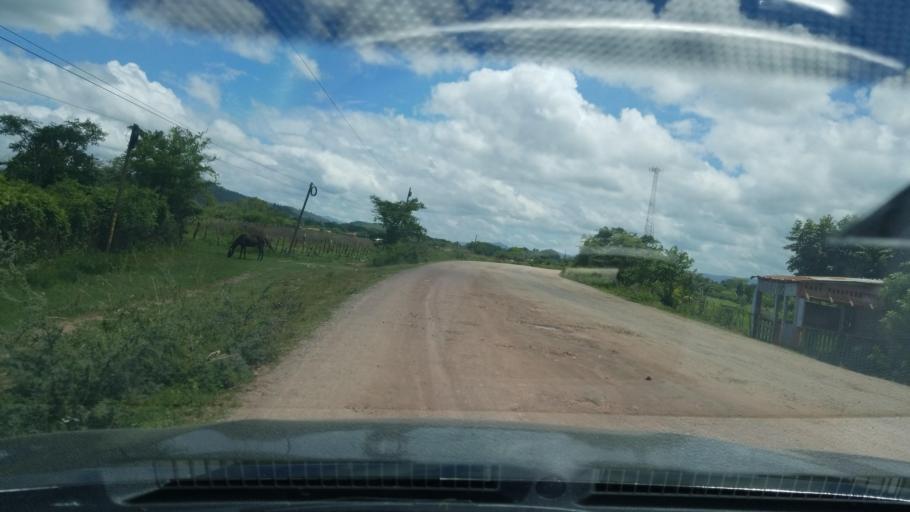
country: HN
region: Francisco Morazan
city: Talanga
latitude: 14.3631
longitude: -87.0519
